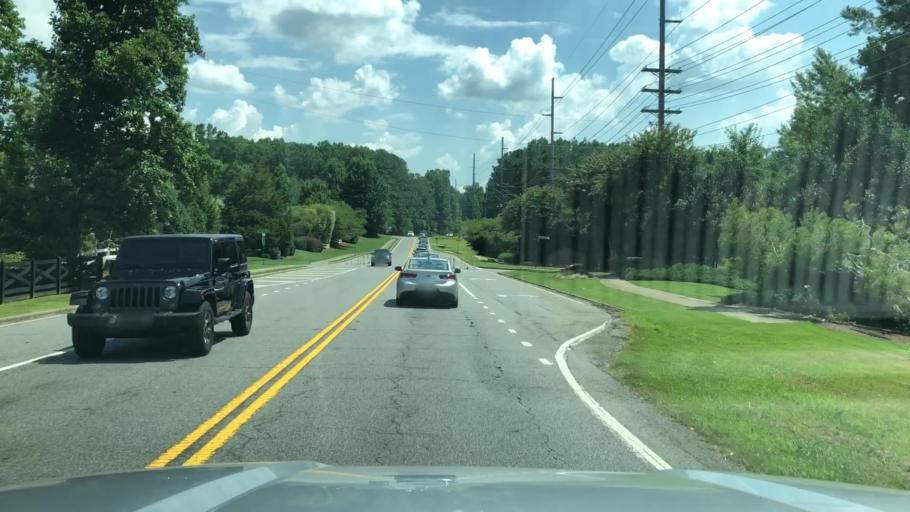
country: US
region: Georgia
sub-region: Cobb County
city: Acworth
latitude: 34.0092
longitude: -84.6990
